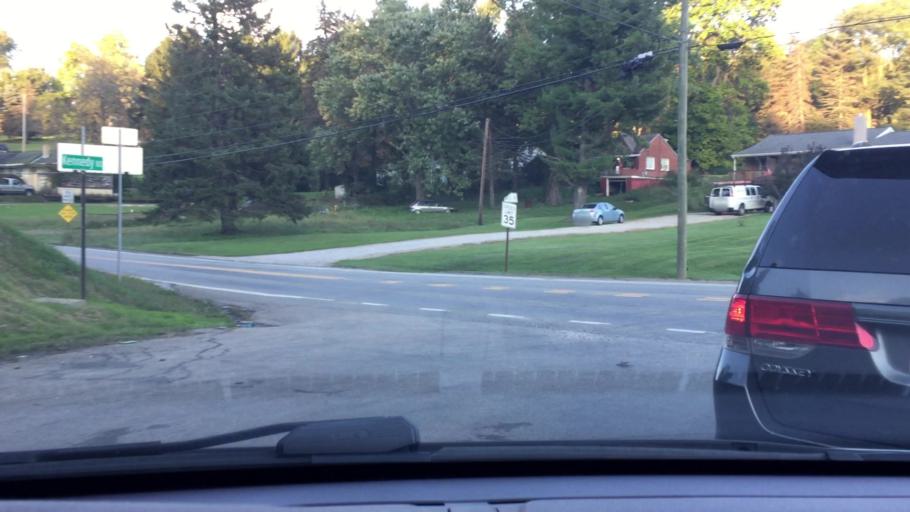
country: US
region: Pennsylvania
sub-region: Washington County
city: Bentleyville
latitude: 40.1268
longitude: -79.9565
